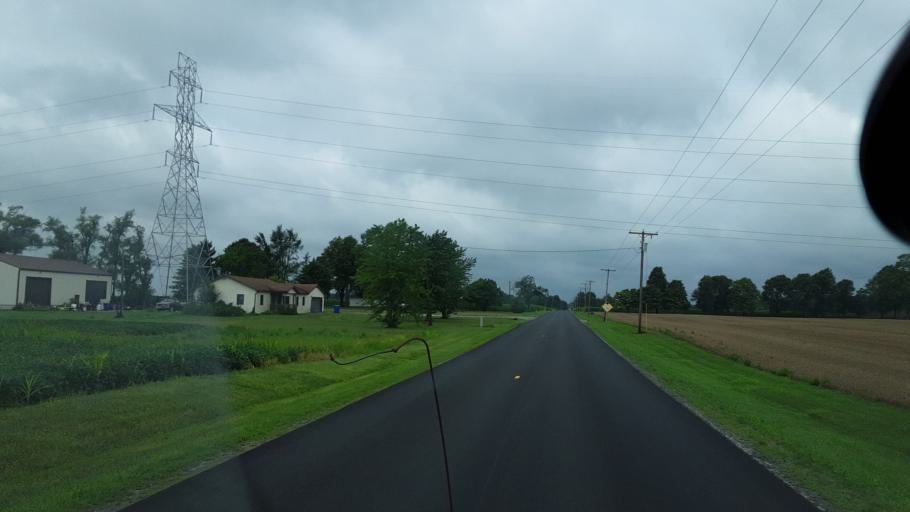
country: US
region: Indiana
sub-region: Allen County
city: Monroeville
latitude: 40.9486
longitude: -84.9705
